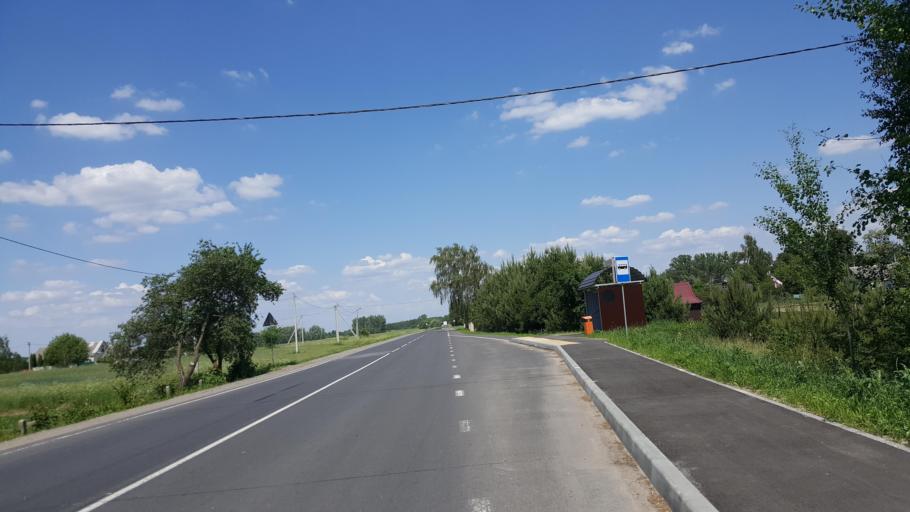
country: BY
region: Brest
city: Kobryn
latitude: 52.2067
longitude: 24.2290
